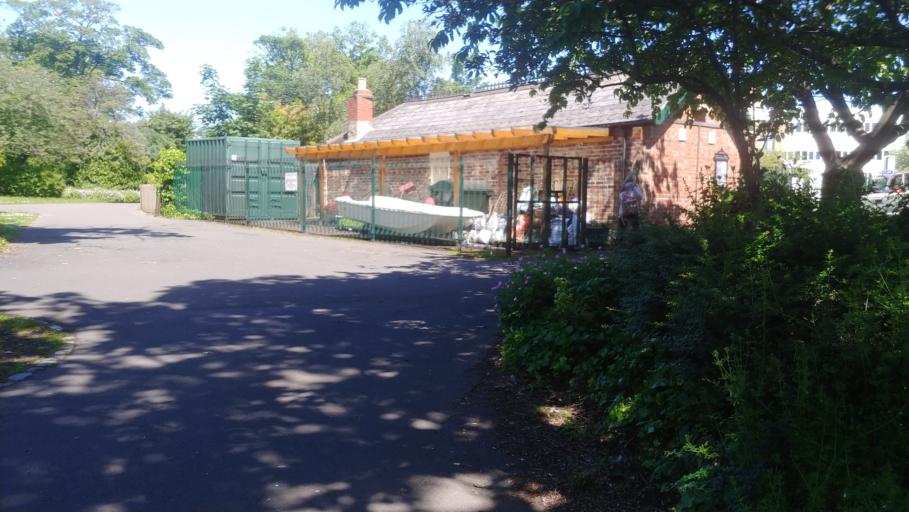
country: GB
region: England
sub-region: Newcastle upon Tyne
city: Newcastle upon Tyne
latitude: 54.9794
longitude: -1.6232
